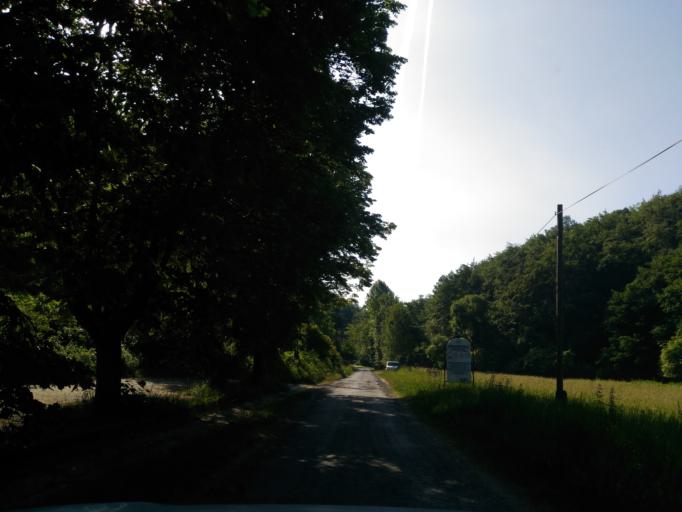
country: HU
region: Baranya
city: Komlo
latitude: 46.2327
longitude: 18.3107
